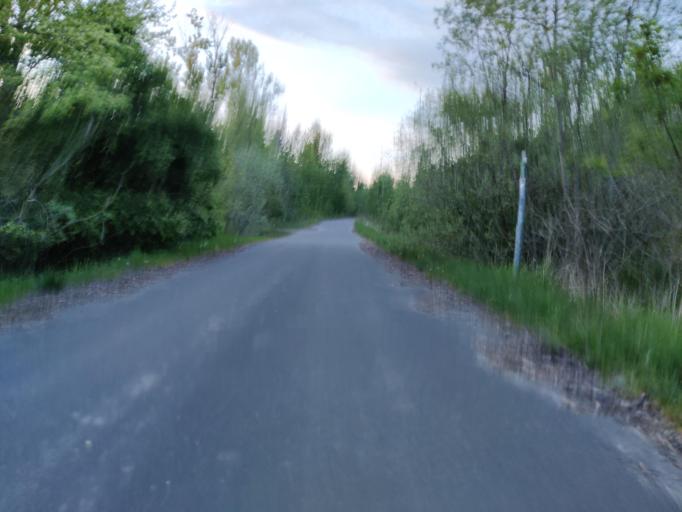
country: DE
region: Saxony
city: Markkleeberg
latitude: 51.2425
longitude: 12.3665
